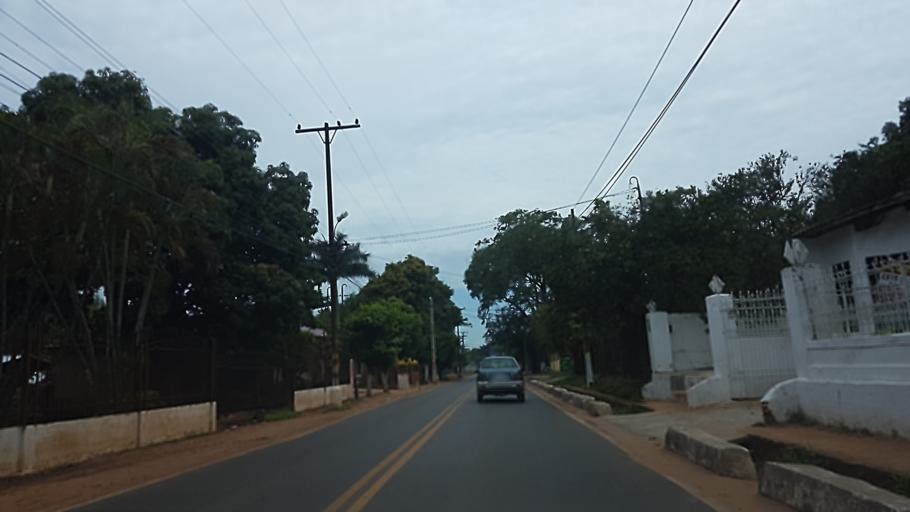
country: PY
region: Central
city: Capiata
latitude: -25.3374
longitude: -57.4611
